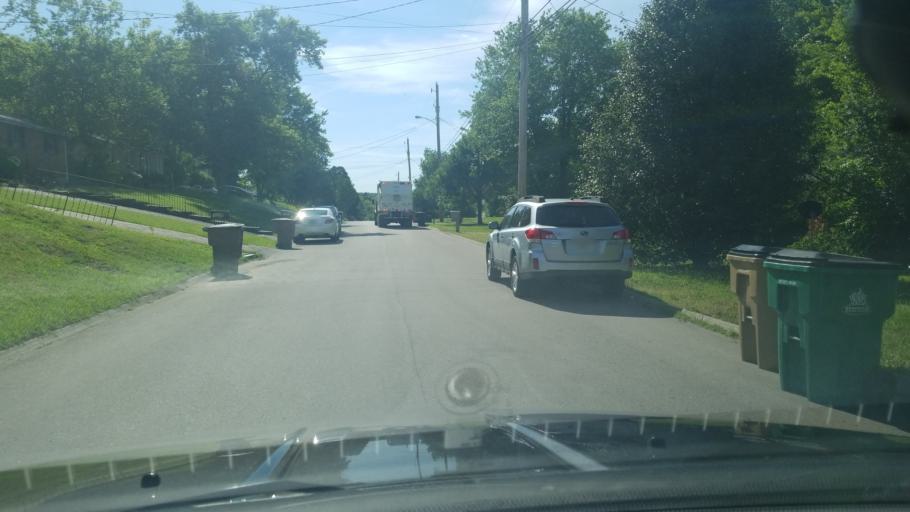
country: US
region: Tennessee
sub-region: Davidson County
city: Nashville
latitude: 36.2365
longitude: -86.7788
